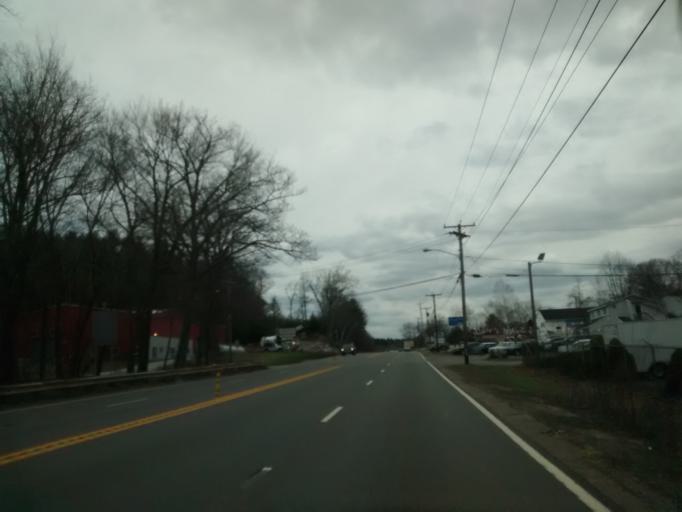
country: US
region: Massachusetts
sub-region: Worcester County
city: Charlton
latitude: 42.1544
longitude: -71.9135
